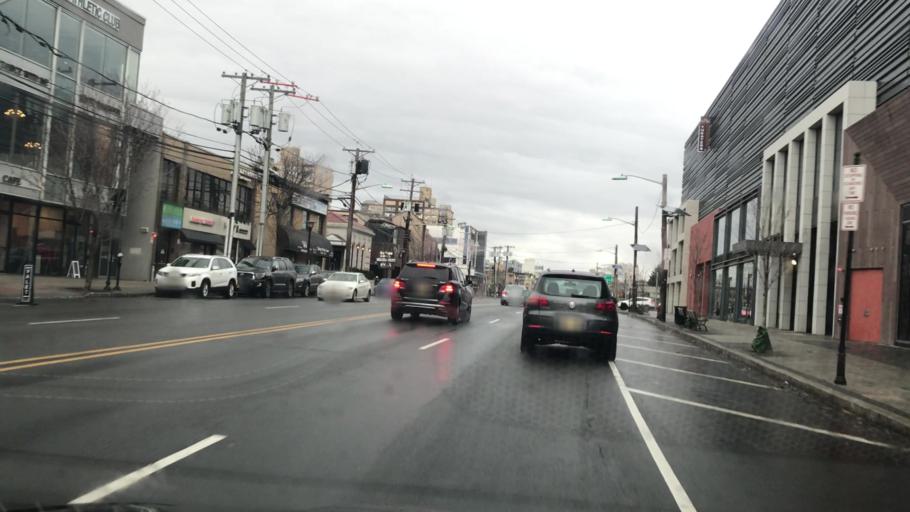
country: US
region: New Jersey
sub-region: Bergen County
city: Fort Lee
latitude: 40.8519
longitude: -73.9695
